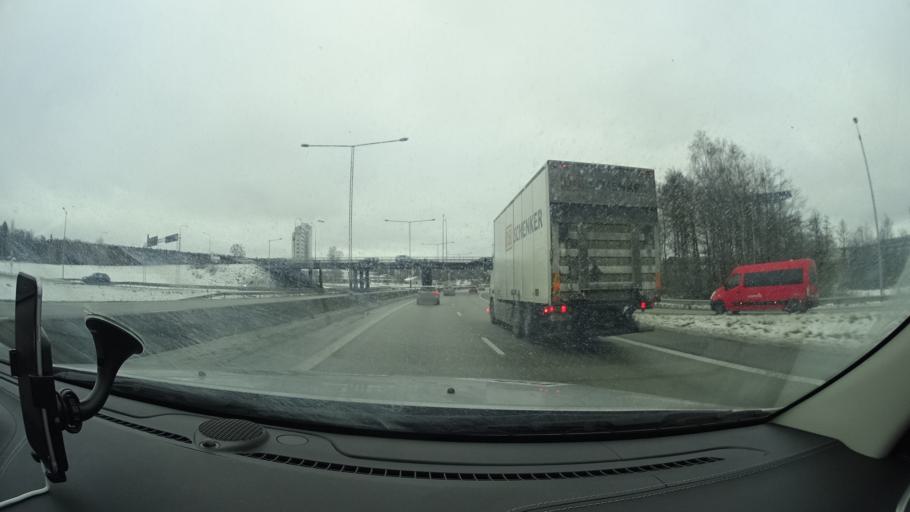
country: SE
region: Joenkoeping
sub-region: Jonkopings Kommun
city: Jonkoping
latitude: 57.7643
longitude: 14.1892
